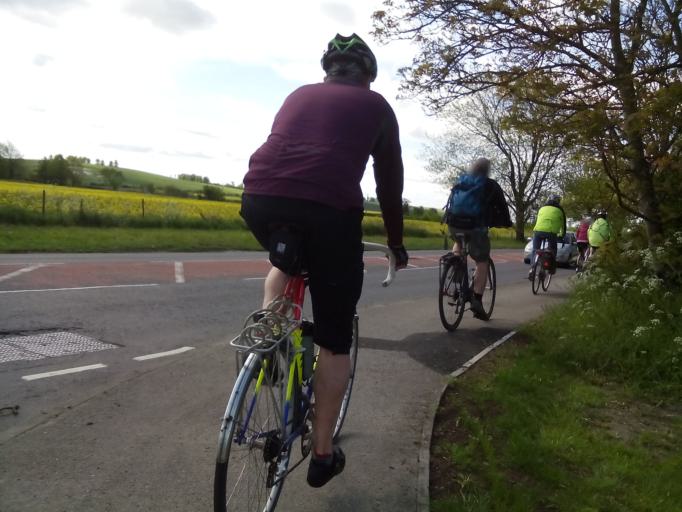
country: GB
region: England
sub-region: Cambridgeshire
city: Harston
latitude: 52.1360
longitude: 0.0746
